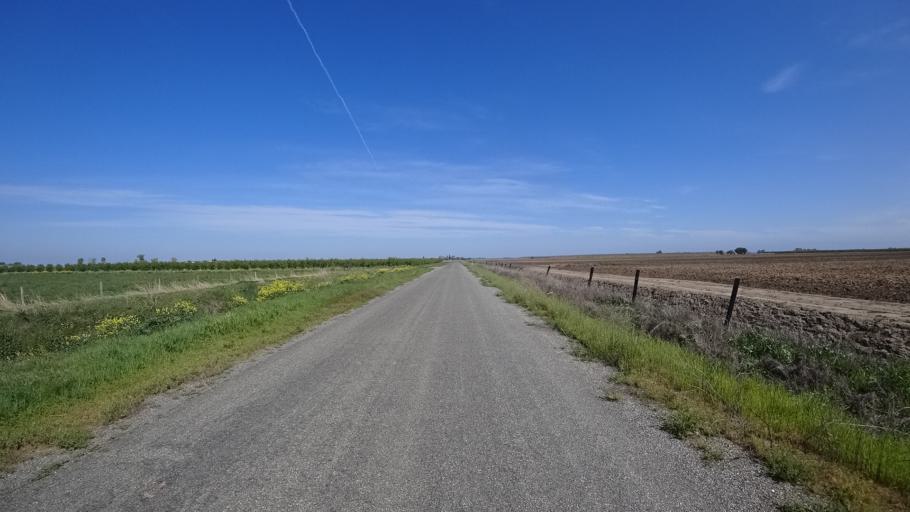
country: US
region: California
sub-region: Glenn County
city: Hamilton City
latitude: 39.6079
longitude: -122.0557
